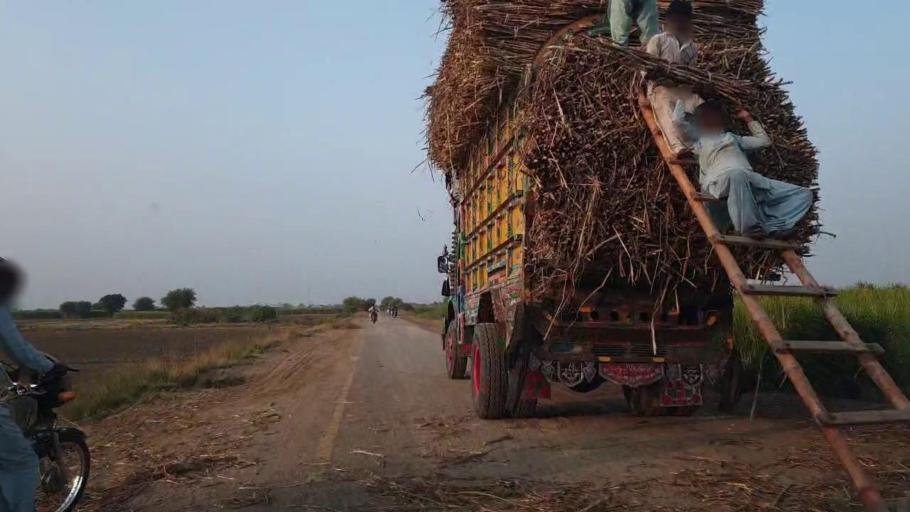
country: PK
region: Sindh
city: Tando Ghulam Ali
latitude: 25.1323
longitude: 68.9587
